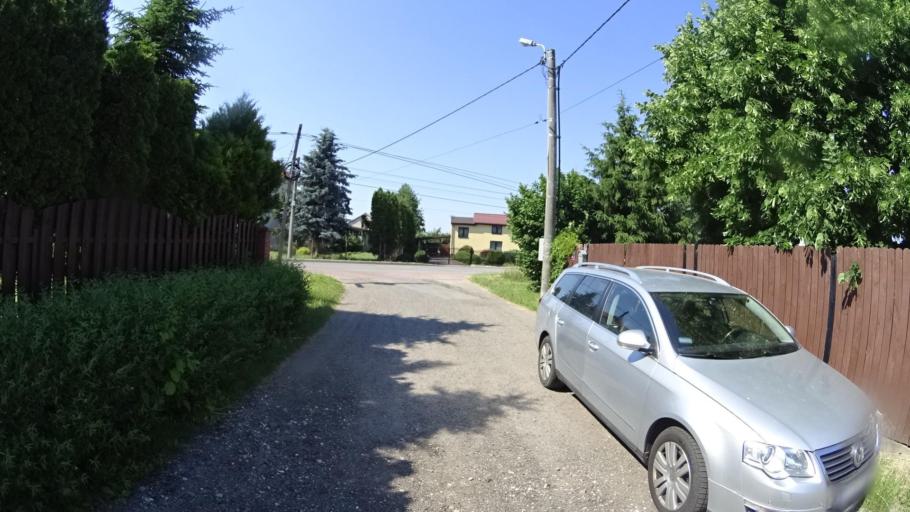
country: PL
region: Masovian Voivodeship
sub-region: Powiat warszawski zachodni
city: Bieniewice
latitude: 52.1971
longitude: 20.5355
